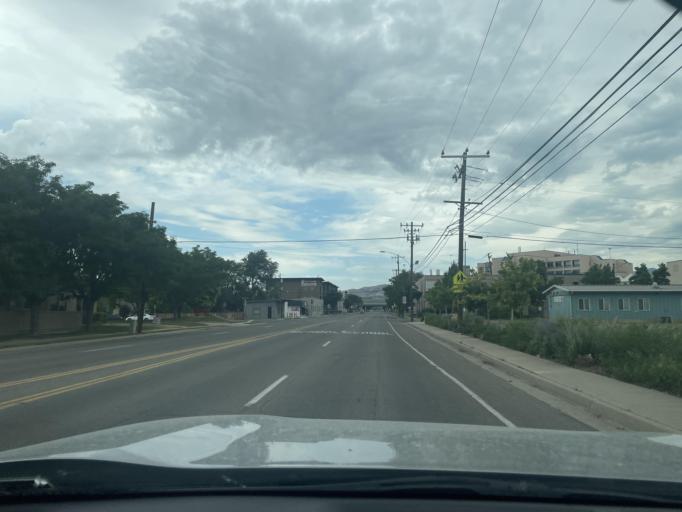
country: US
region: Utah
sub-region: Salt Lake County
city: South Salt Lake
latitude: 40.7136
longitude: -111.8911
